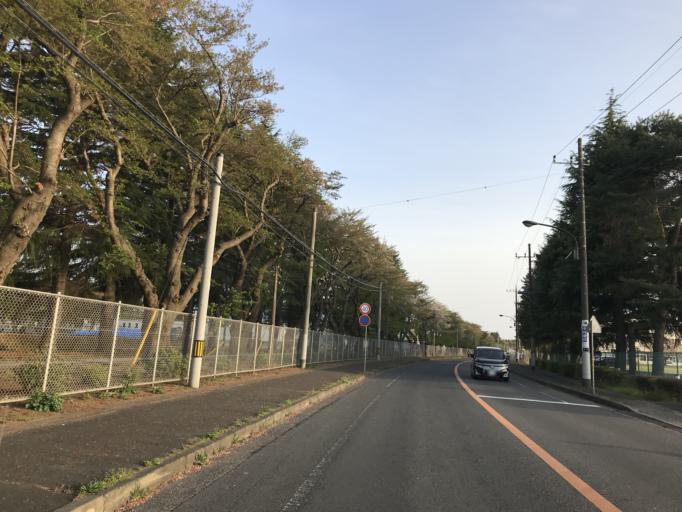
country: JP
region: Ibaraki
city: Katsuta
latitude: 36.3846
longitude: 140.5276
